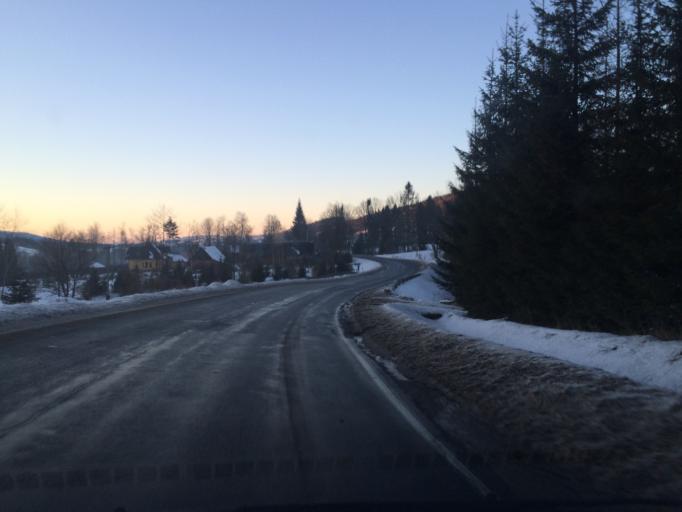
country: PL
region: Subcarpathian Voivodeship
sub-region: Powiat bieszczadzki
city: Czarna
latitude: 49.3535
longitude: 22.6807
